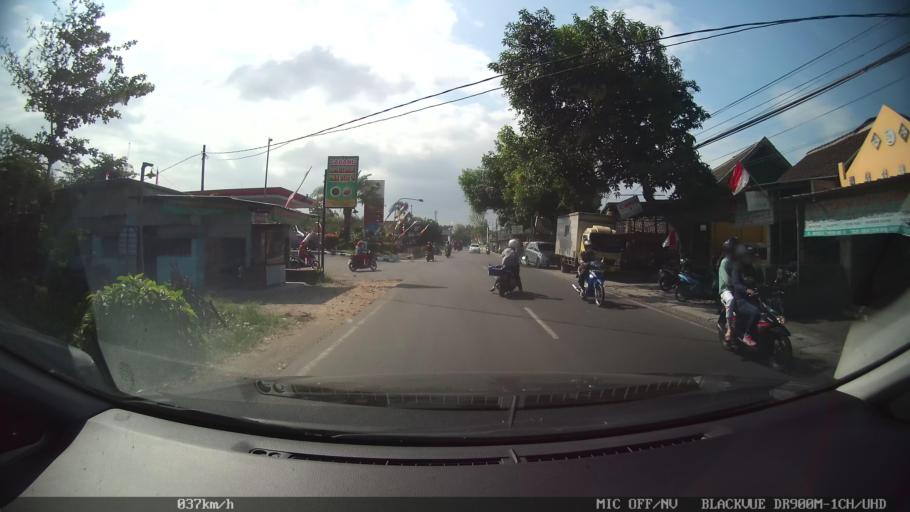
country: ID
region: Daerah Istimewa Yogyakarta
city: Sewon
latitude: -7.8656
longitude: 110.3899
